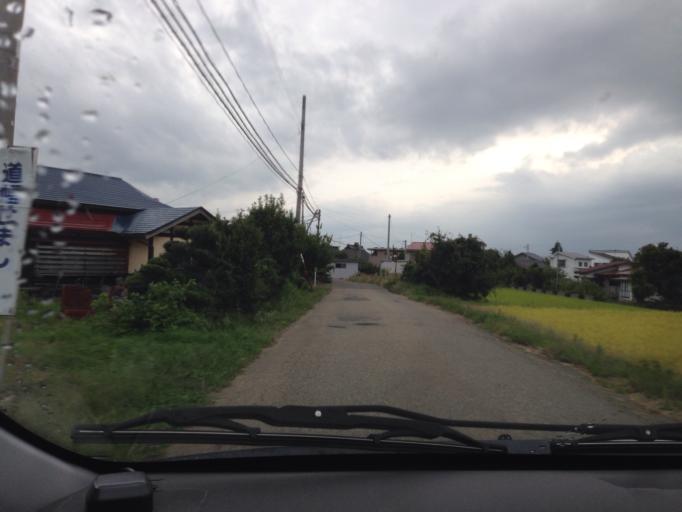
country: JP
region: Fukushima
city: Kitakata
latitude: 37.5987
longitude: 139.8983
